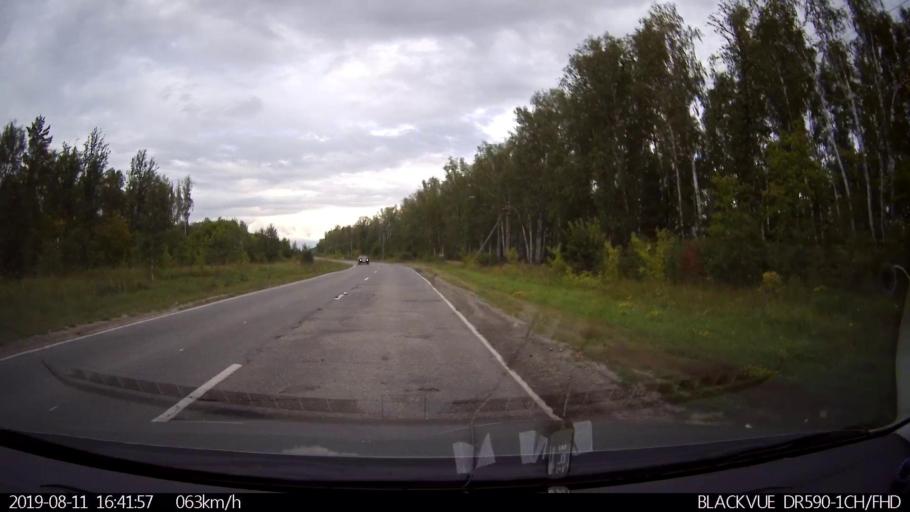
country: RU
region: Ulyanovsk
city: Mayna
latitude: 54.1569
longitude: 47.6579
